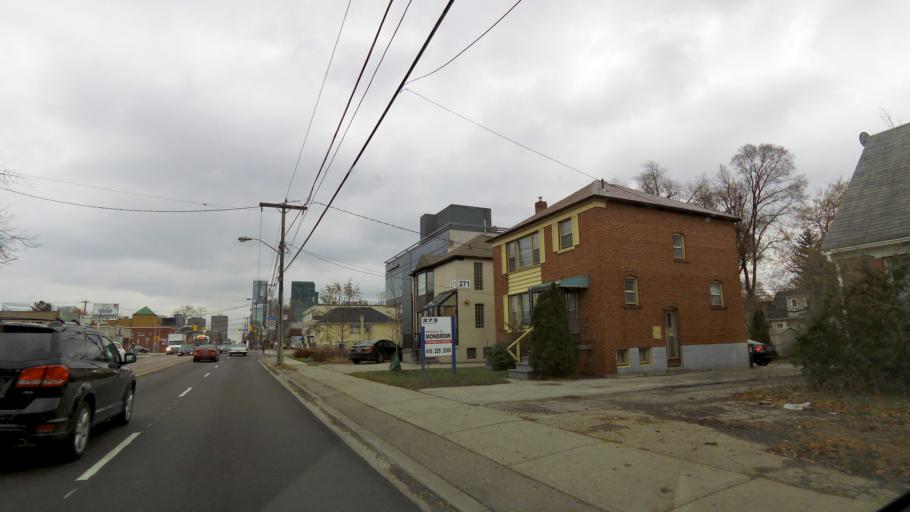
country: CA
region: Ontario
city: North York
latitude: 43.7585
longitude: -79.4242
